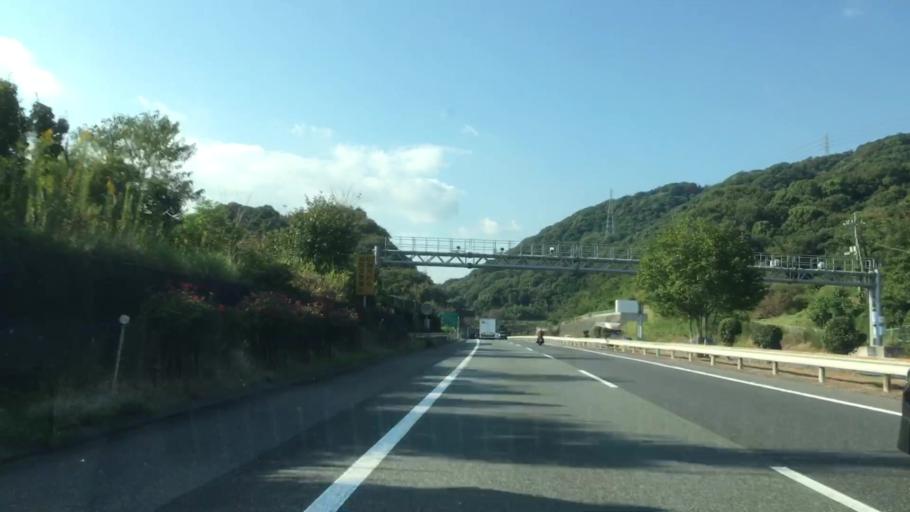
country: JP
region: Yamaguchi
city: Tokuyama
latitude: 34.0570
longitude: 131.8389
